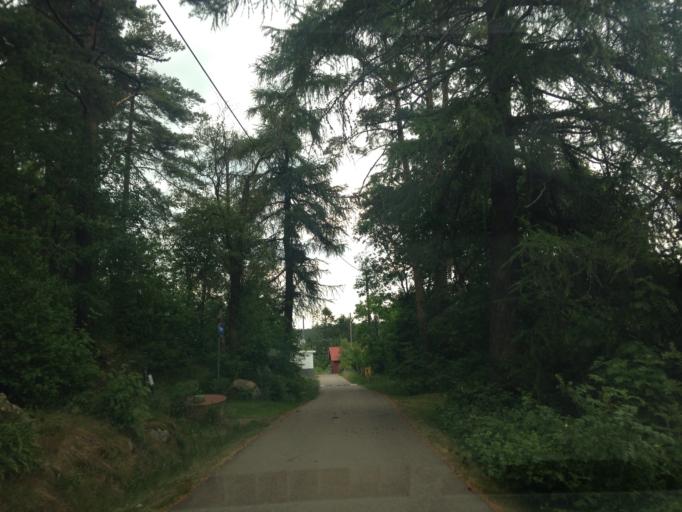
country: SE
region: Vaestra Goetaland
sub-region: Goteborg
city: Goeteborg
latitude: 57.7834
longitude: 11.9317
